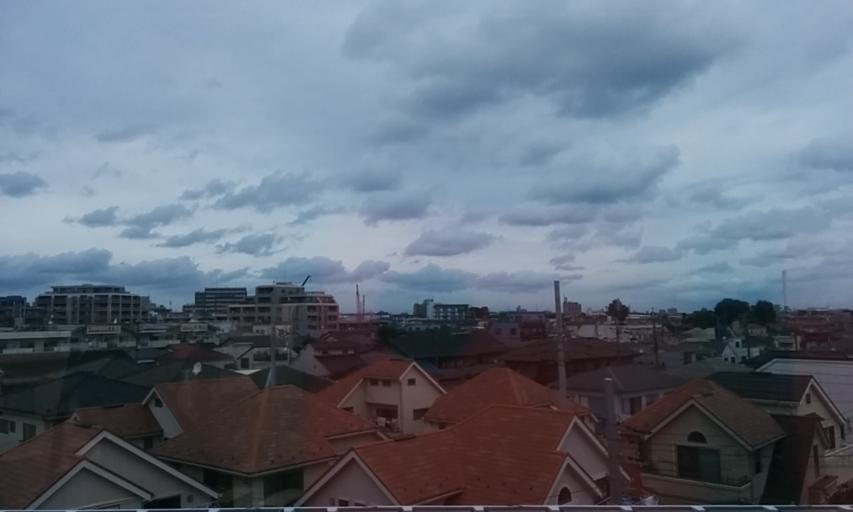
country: JP
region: Saitama
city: Wako
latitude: 35.7457
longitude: 139.5968
